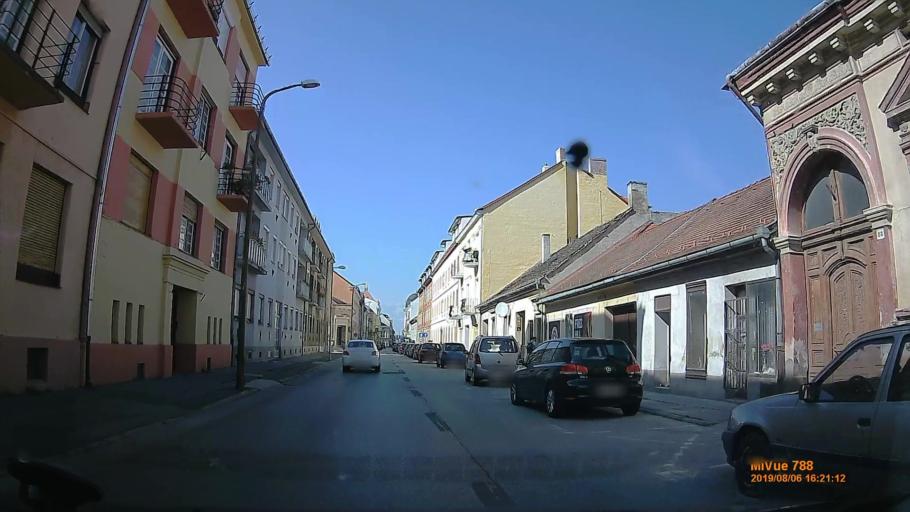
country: HU
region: Zala
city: Nagykanizsa
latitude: 46.4521
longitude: 16.9917
